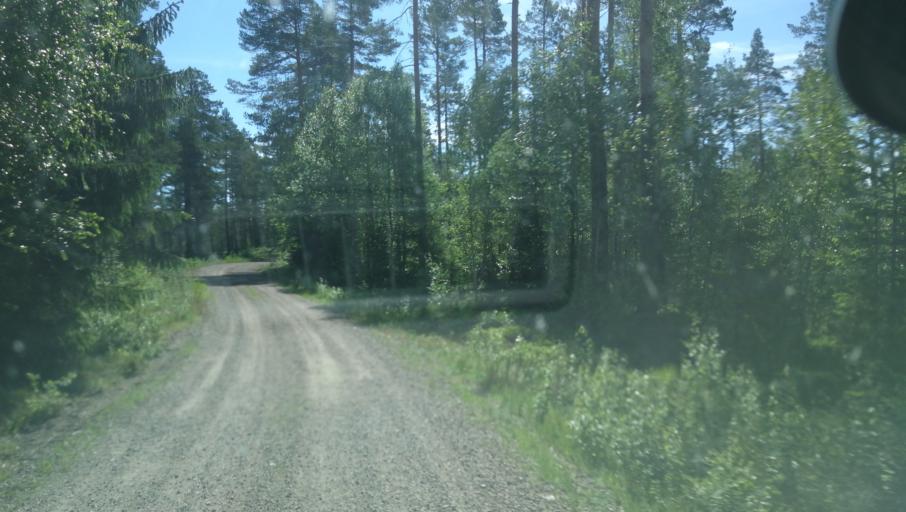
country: SE
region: Dalarna
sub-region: Vansbro Kommun
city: Vansbro
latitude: 60.8234
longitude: 14.1891
